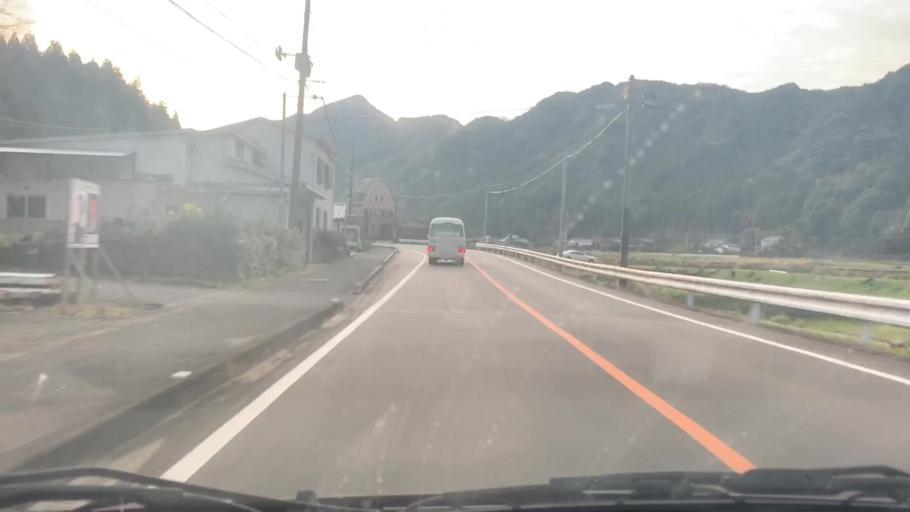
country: JP
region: Saga Prefecture
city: Kashima
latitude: 33.0834
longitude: 130.0715
